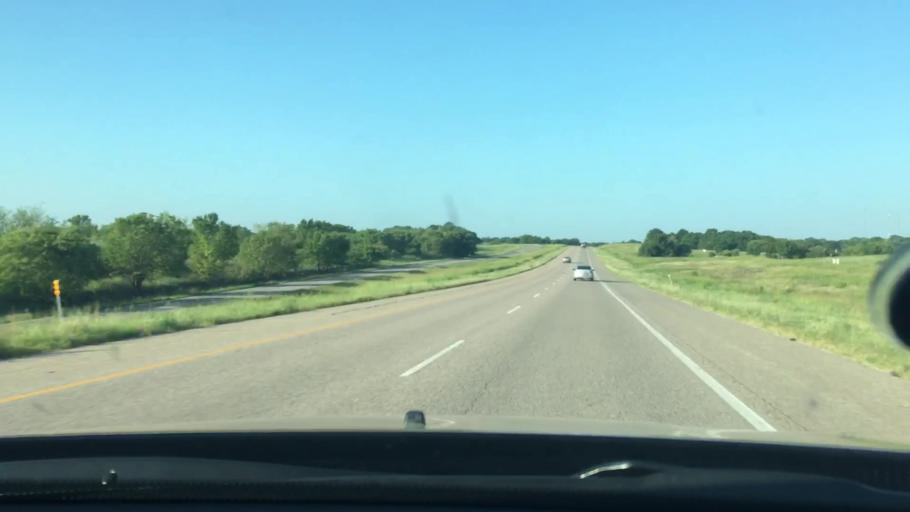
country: US
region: Oklahoma
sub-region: Pontotoc County
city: Ada
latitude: 34.6978
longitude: -96.7373
